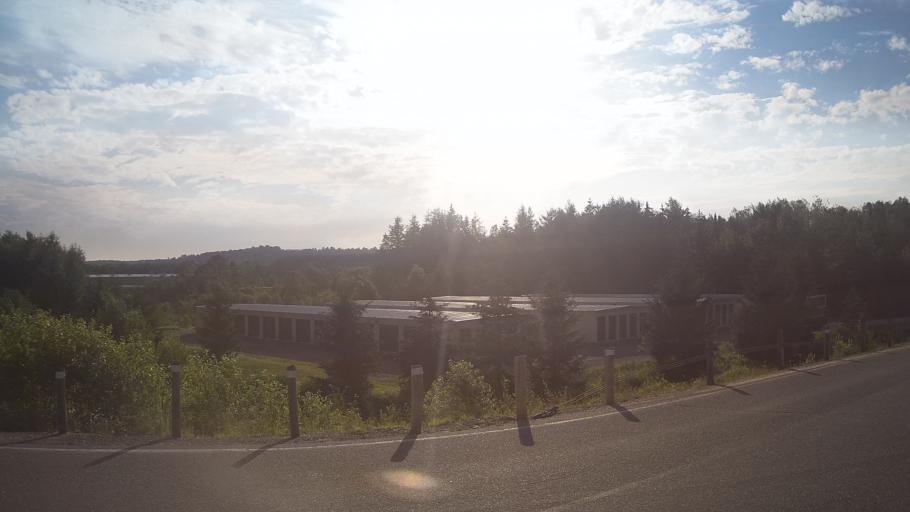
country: CA
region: Ontario
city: Huntsville
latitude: 45.3734
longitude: -79.2144
